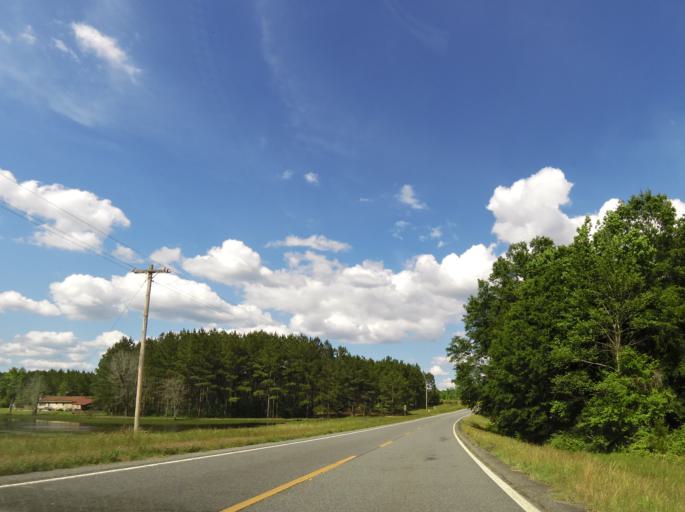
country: US
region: Georgia
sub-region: Treutlen County
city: Soperton
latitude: 32.3327
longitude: -82.6643
